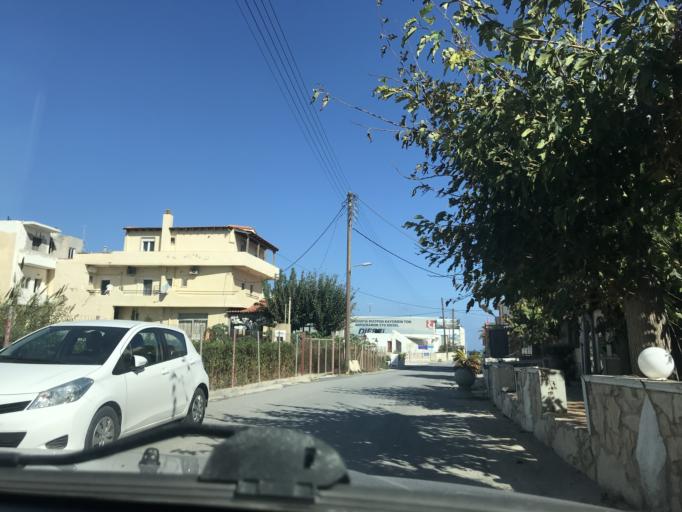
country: GR
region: Crete
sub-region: Nomos Irakleiou
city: Gazi
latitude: 35.3369
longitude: 25.0677
